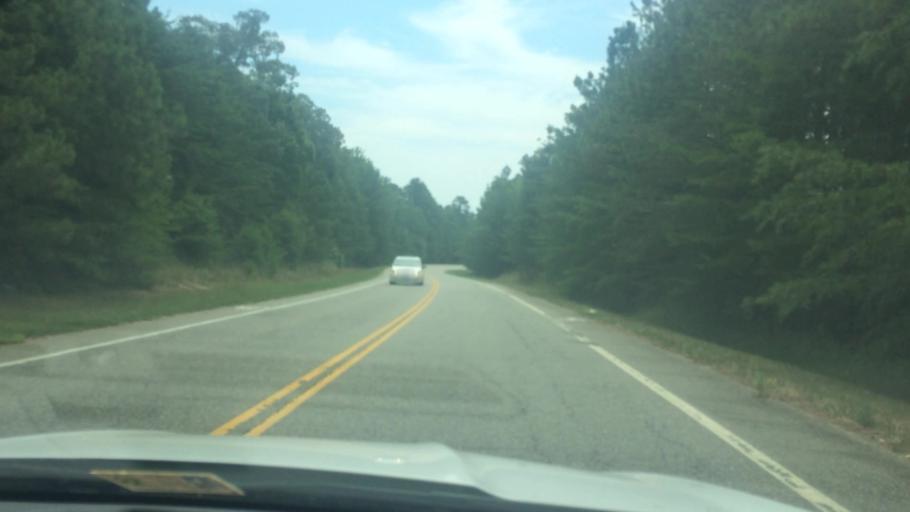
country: US
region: Virginia
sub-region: James City County
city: Williamsburg
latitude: 37.2691
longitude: -76.8072
